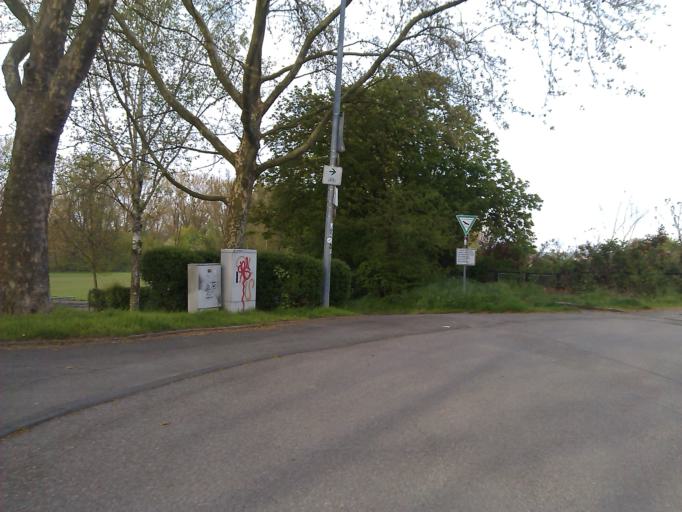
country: DE
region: Baden-Wuerttemberg
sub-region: Regierungsbezirk Stuttgart
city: Nordheim
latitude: 49.1182
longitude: 9.1656
